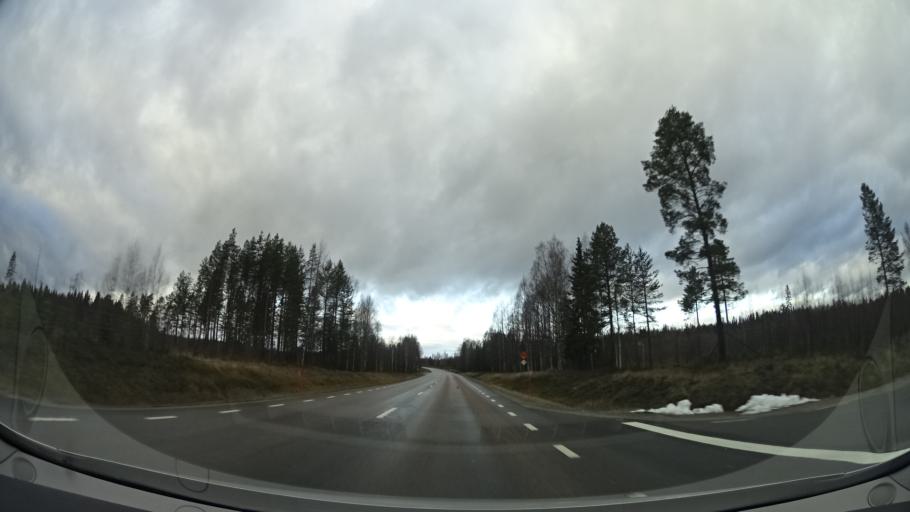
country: SE
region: Vaesterbotten
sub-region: Skelleftea Kommun
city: Viken
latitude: 64.7968
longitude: 20.7414
